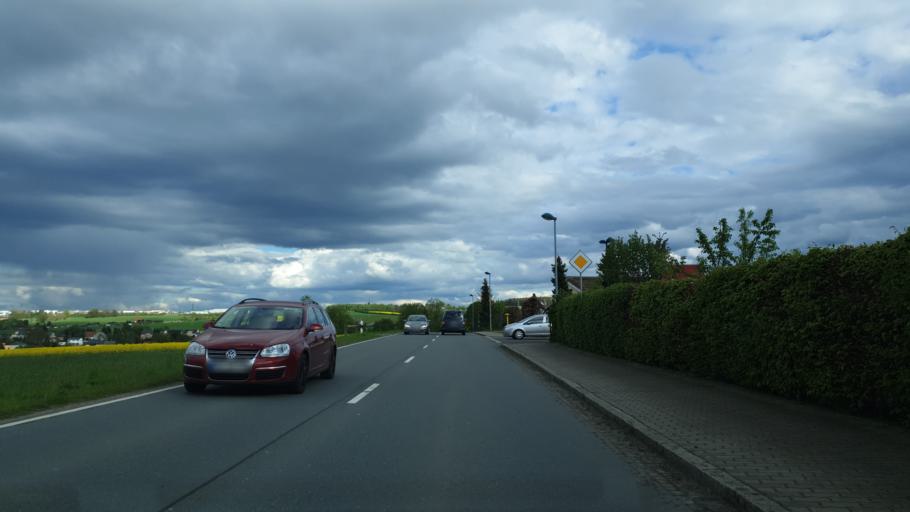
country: DE
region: Saxony
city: Oelsnitz
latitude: 50.7122
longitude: 12.7293
